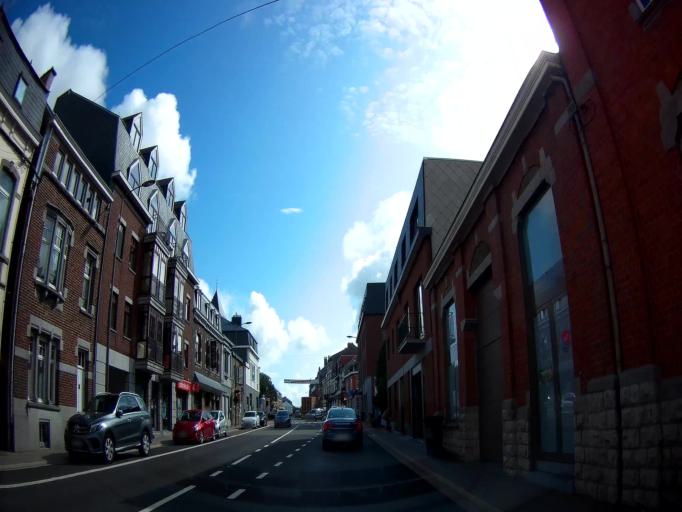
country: BE
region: Wallonia
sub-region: Province de Liege
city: Herve
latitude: 50.6475
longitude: 5.8193
